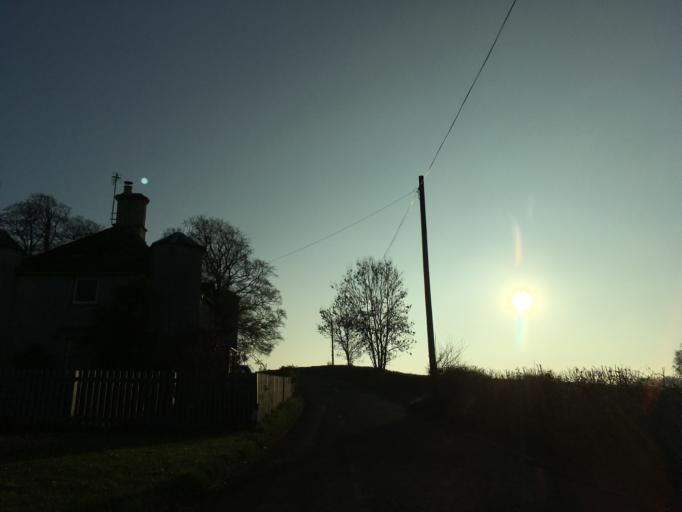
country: GB
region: England
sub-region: Wiltshire
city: Luckington
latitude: 51.5533
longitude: -2.2924
